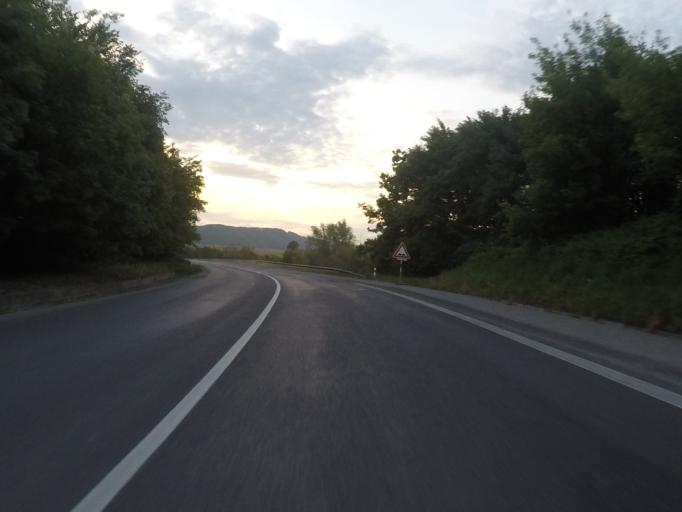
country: SK
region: Banskobystricky
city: Rimavska Sobota
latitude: 48.4753
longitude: 19.9496
